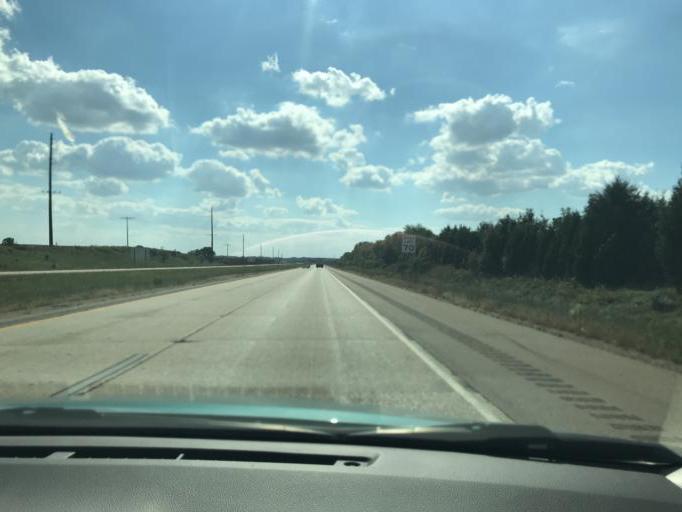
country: US
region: Wisconsin
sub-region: Walworth County
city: Delavan
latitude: 42.6216
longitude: -88.6274
